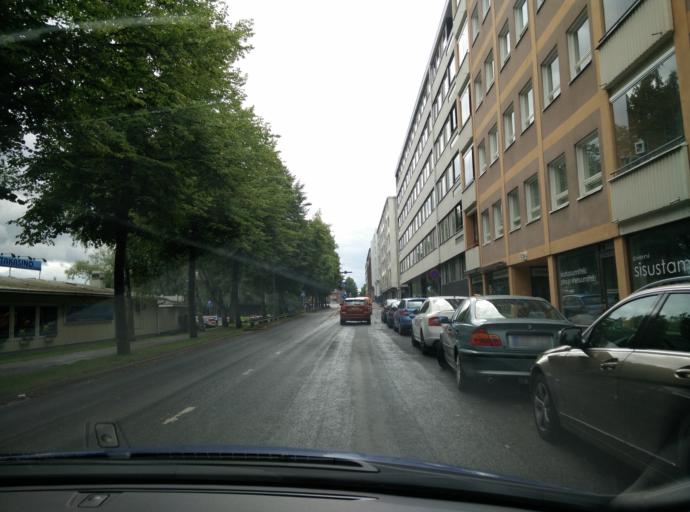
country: FI
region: Haeme
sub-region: Haemeenlinna
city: Haemeenlinna
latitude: 60.9989
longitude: 24.4698
